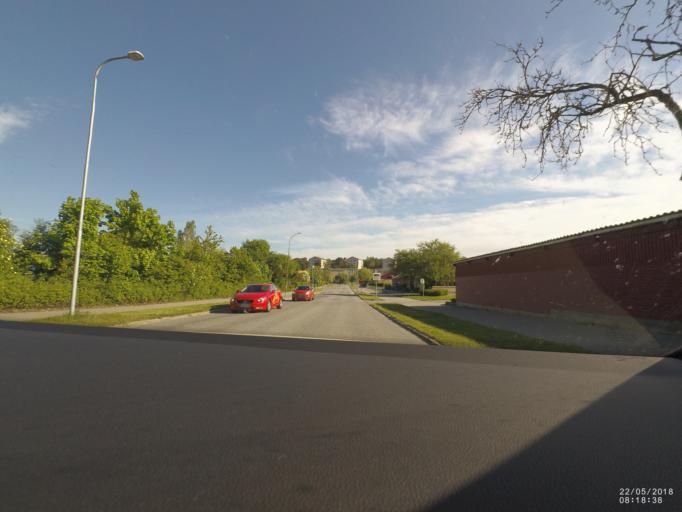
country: SE
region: Soedermanland
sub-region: Nykopings Kommun
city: Nykoping
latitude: 58.7521
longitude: 17.0435
